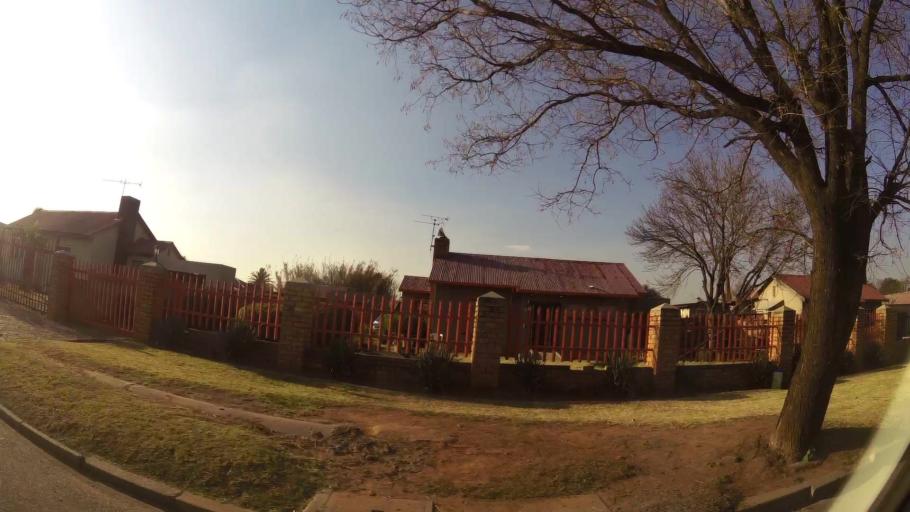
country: ZA
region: Gauteng
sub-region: Ekurhuleni Metropolitan Municipality
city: Springs
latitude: -26.2572
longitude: 28.3864
